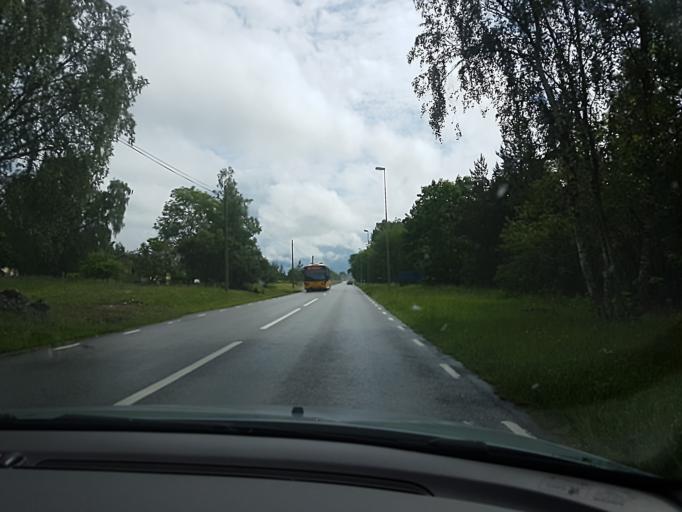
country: SE
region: Uppsala
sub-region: Osthammars Kommun
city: OEsthammar
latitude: 60.2941
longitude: 18.2845
